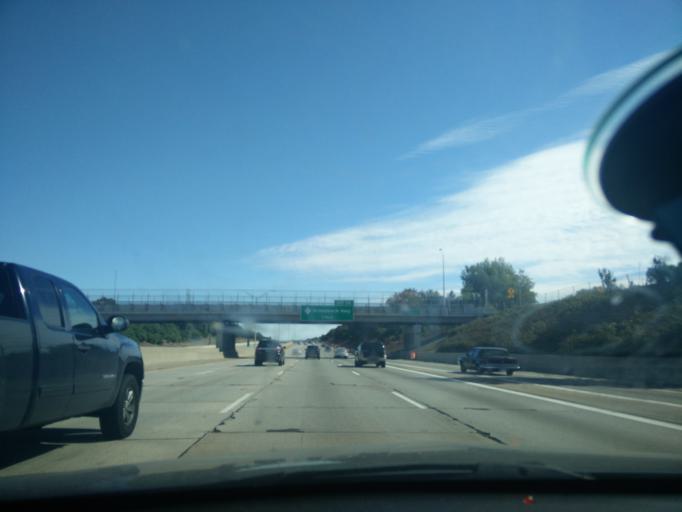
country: US
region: Michigan
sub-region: Macomb County
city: Center Line
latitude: 42.4920
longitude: -83.0023
